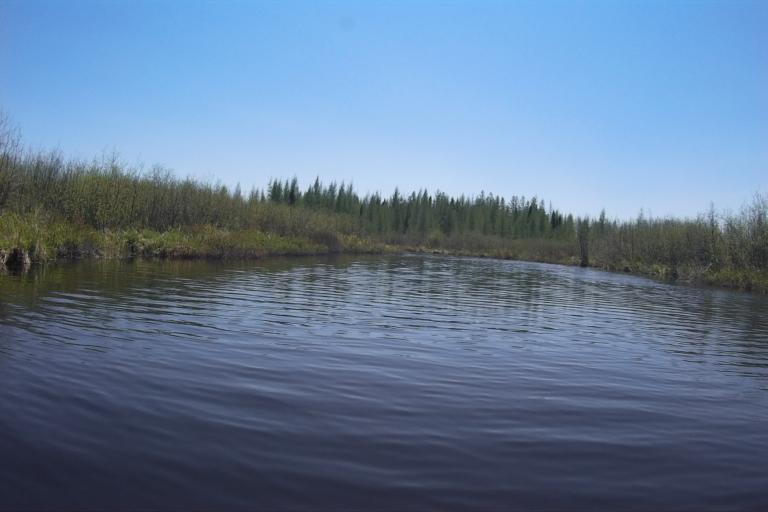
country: CA
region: Ontario
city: Powassan
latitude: 46.1583
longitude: -79.2549
